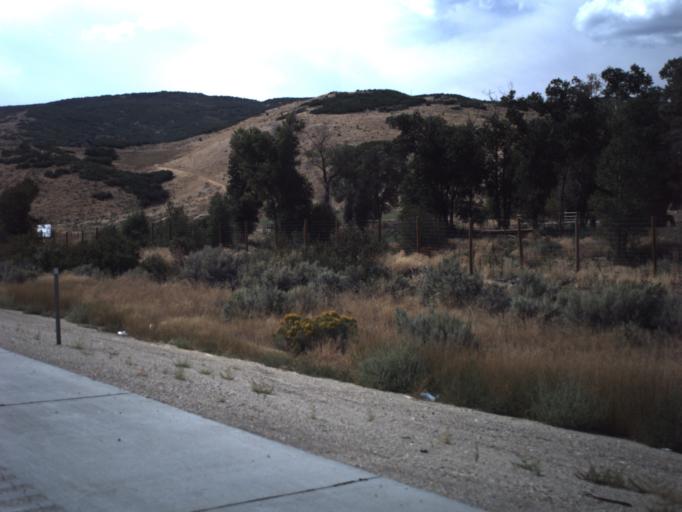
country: US
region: Utah
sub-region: Summit County
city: Coalville
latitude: 40.8052
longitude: -111.4351
